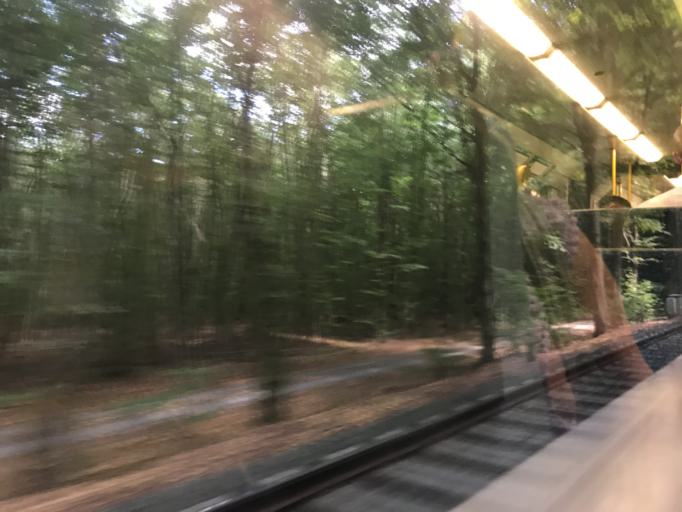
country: DE
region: Hesse
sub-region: Regierungsbezirk Darmstadt
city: Neu Isenburg
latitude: 50.0653
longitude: 8.6897
